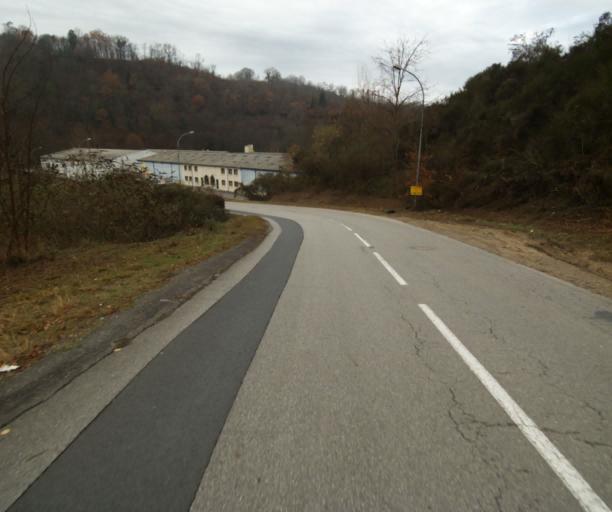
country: FR
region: Limousin
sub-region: Departement de la Correze
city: Chameyrat
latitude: 45.2407
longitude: 1.7368
